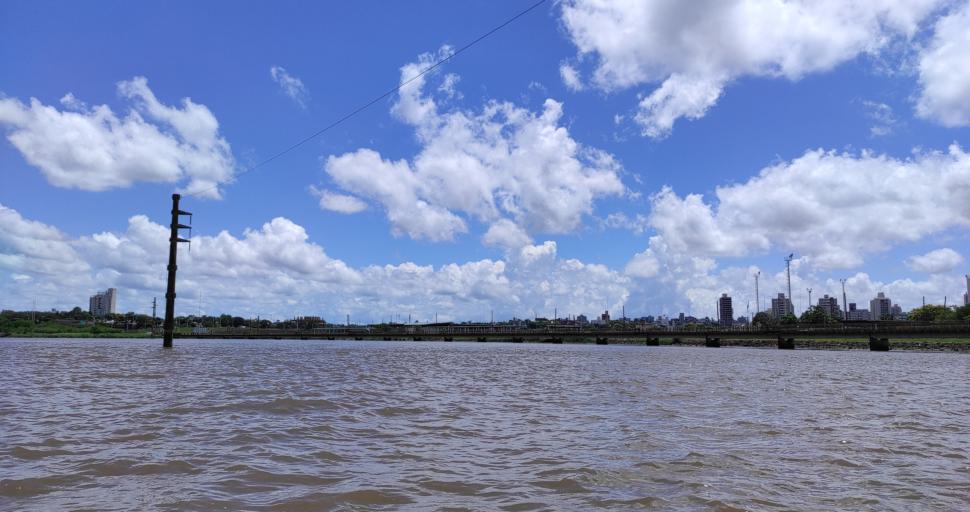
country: AR
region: Misiones
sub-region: Departamento de Capital
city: Posadas
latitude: -27.3772
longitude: -55.8795
